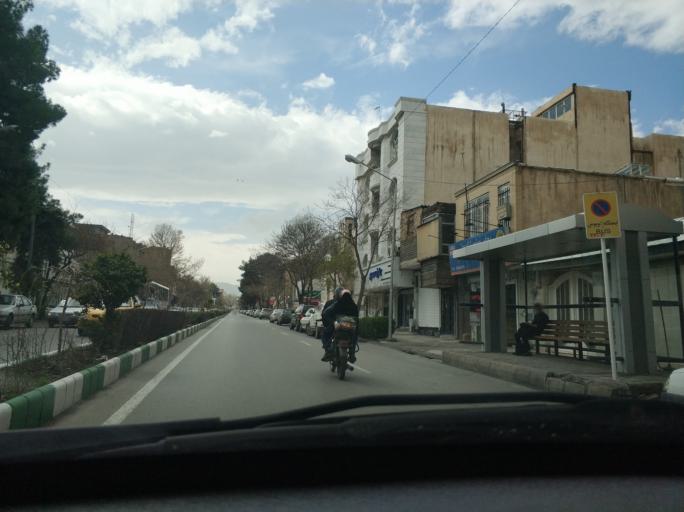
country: IR
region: Razavi Khorasan
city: Mashhad
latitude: 36.2844
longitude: 59.5773
